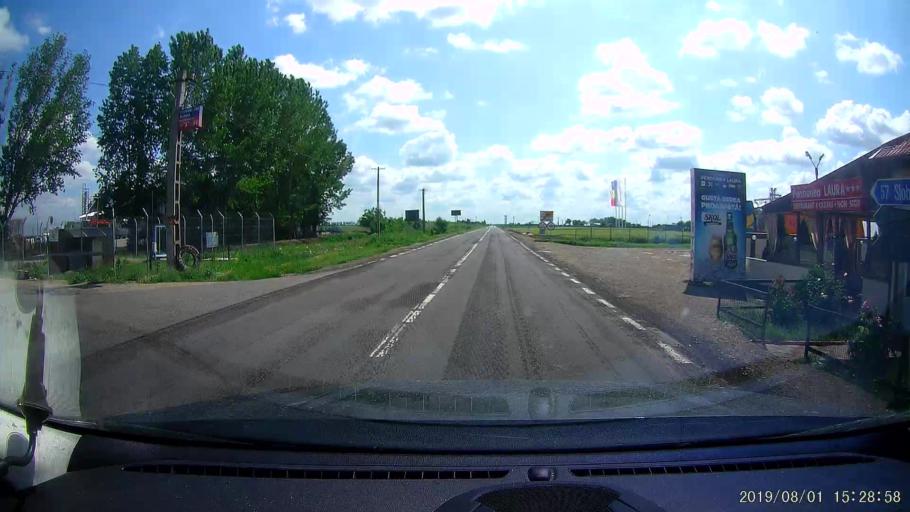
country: RO
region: Braila
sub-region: Comuna Viziru
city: Viziru
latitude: 44.9889
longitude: 27.7041
